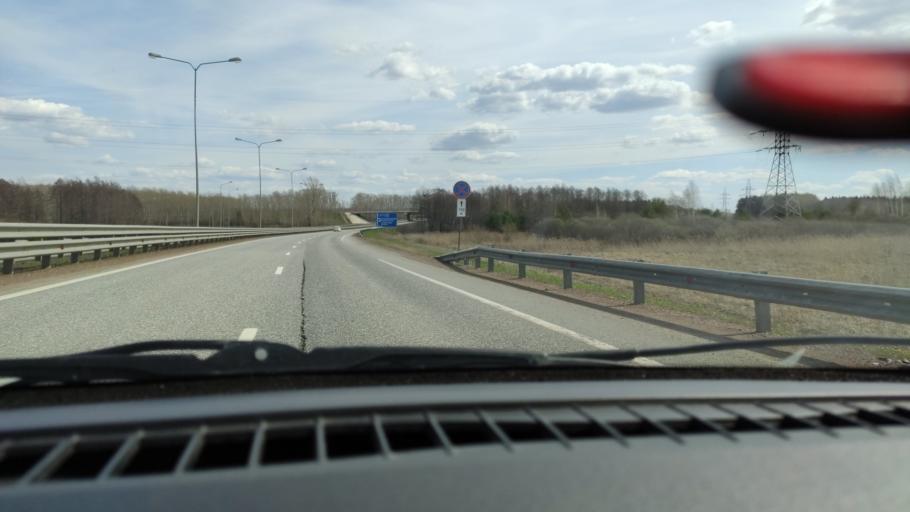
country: RU
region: Bashkortostan
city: Kushnarenkovo
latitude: 55.0587
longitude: 55.4286
